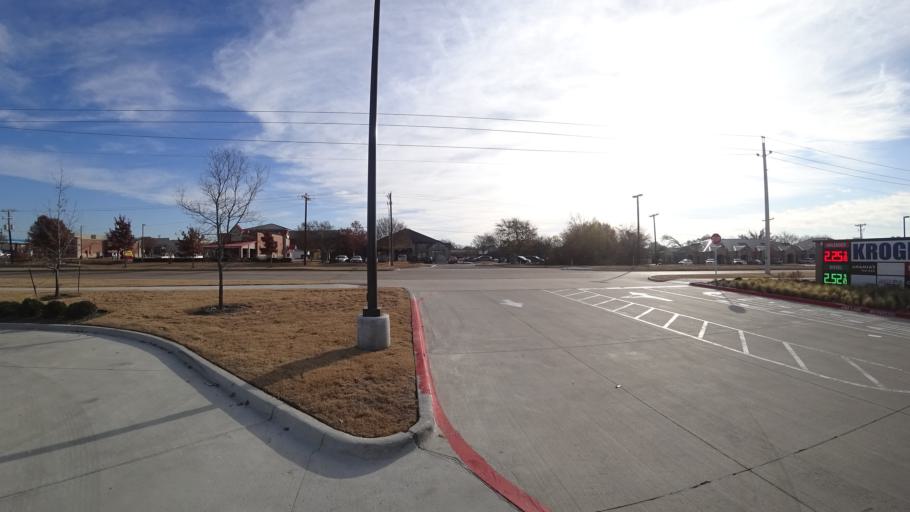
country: US
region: Texas
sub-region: Collin County
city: McKinney
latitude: 33.2167
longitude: -96.6798
